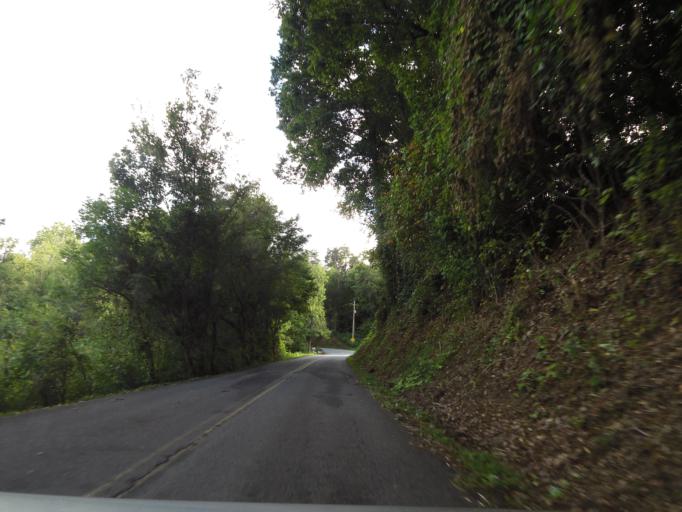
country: US
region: Tennessee
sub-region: Grainger County
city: Blaine
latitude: 36.1252
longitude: -83.7465
